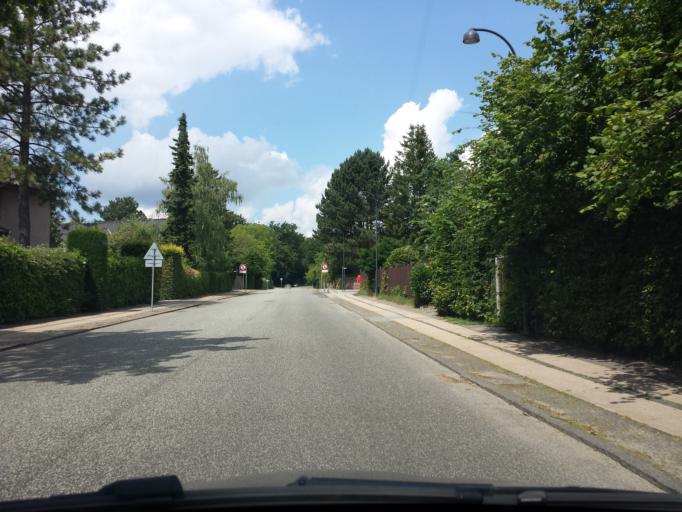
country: DK
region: Capital Region
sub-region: Gentofte Kommune
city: Charlottenlund
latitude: 55.7668
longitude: 12.5676
